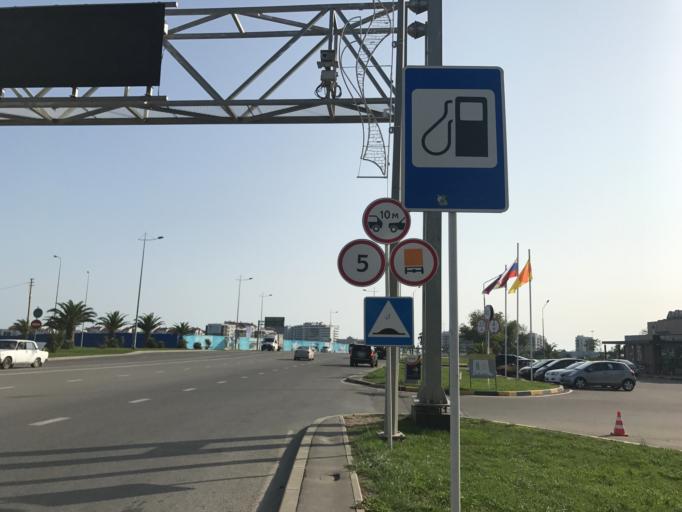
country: RU
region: Krasnodarskiy
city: Adler
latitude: 43.4174
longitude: 39.9402
